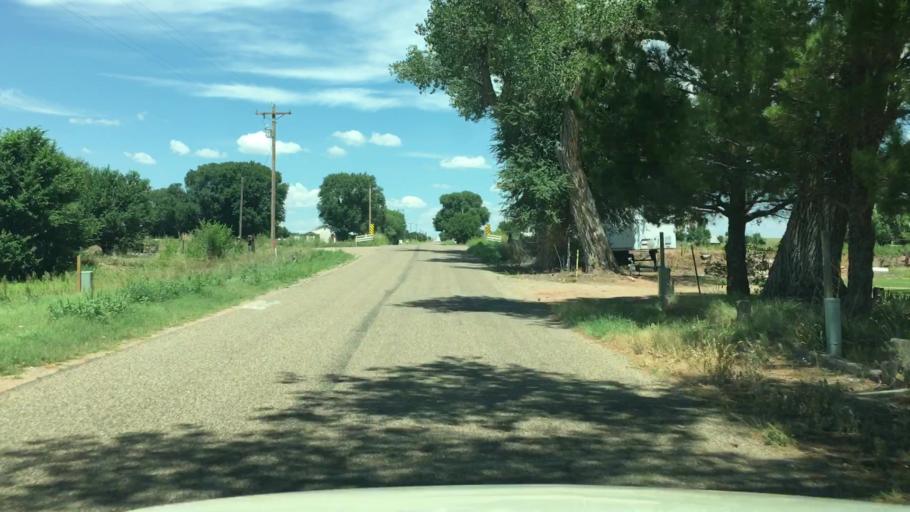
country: US
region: New Mexico
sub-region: De Baca County
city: Fort Sumner
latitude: 34.4392
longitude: -104.1936
